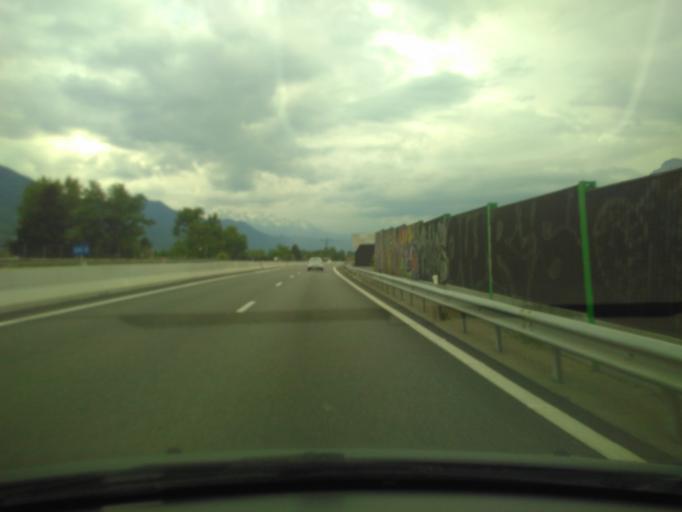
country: FR
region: Rhone-Alpes
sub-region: Departement de l'Isere
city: Pontcharra
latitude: 45.4366
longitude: 6.0033
